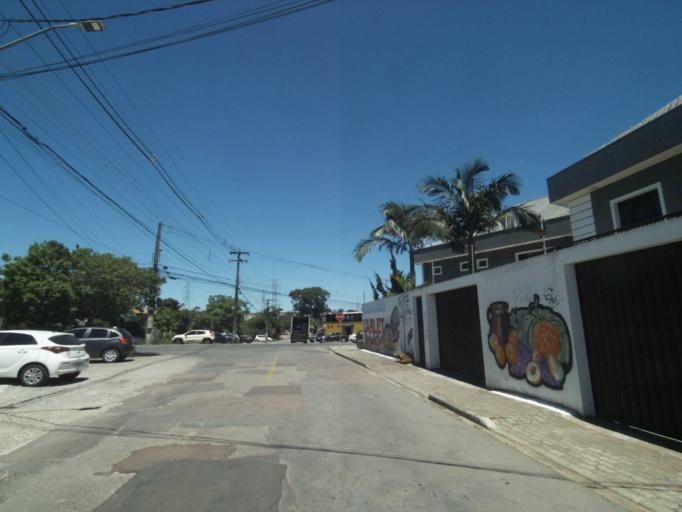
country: BR
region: Parana
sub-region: Curitiba
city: Curitiba
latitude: -25.4756
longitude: -49.3389
